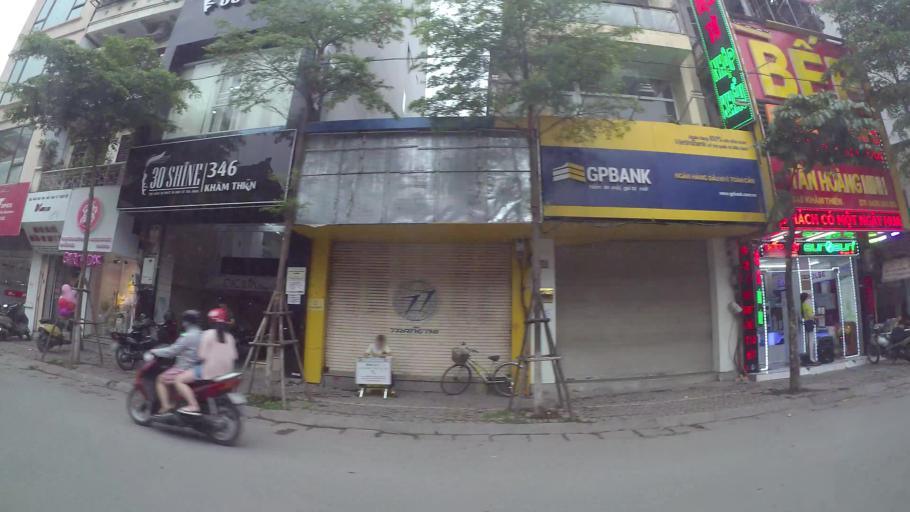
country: VN
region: Ha Noi
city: Dong Da
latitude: 21.0196
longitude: 105.8324
